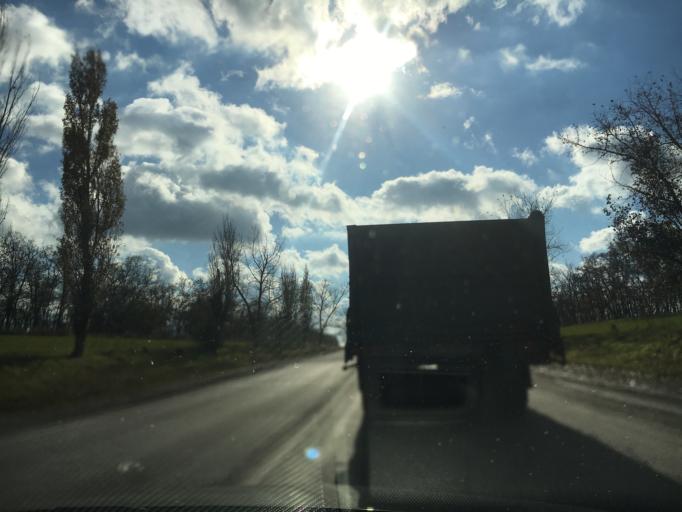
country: RU
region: Rostov
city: Matveyev Kurgan
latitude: 47.5427
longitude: 38.8912
